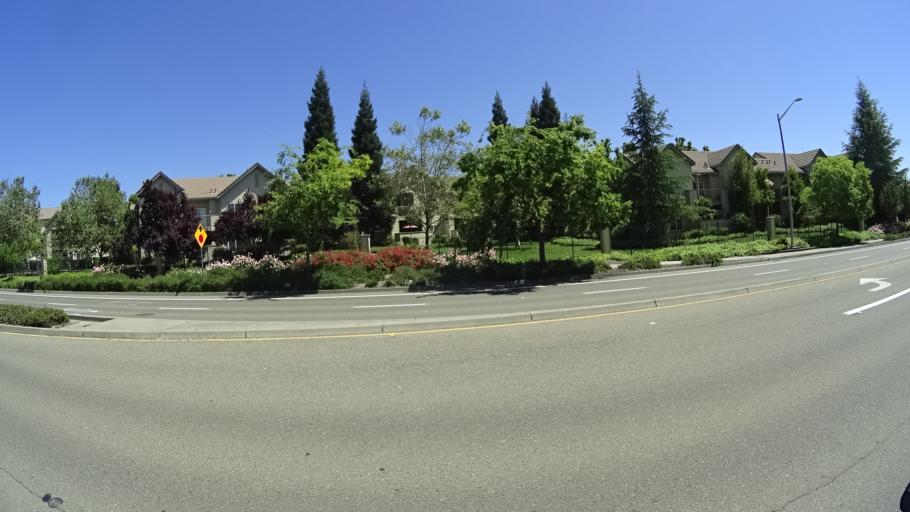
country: US
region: California
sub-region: Placer County
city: Roseville
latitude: 38.7991
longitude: -121.2855
